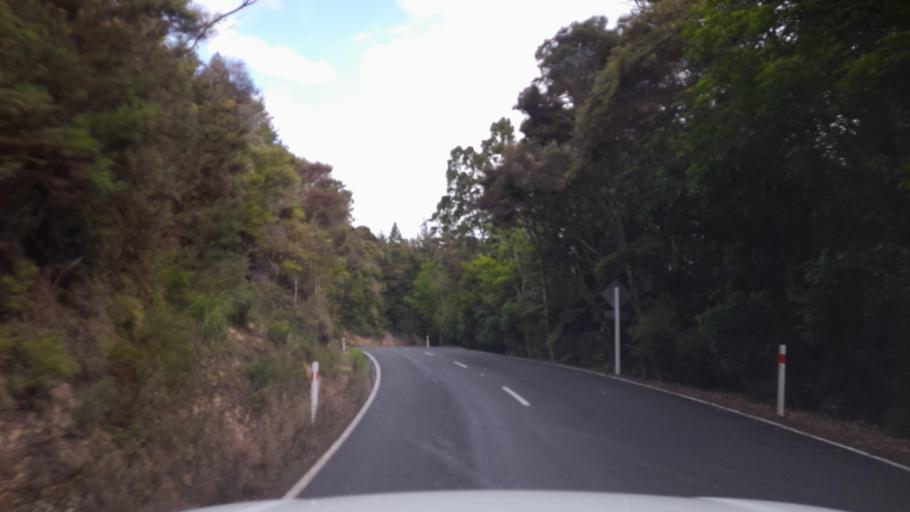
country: NZ
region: Northland
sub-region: Whangarei
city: Maungatapere
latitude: -35.7634
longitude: 174.2421
